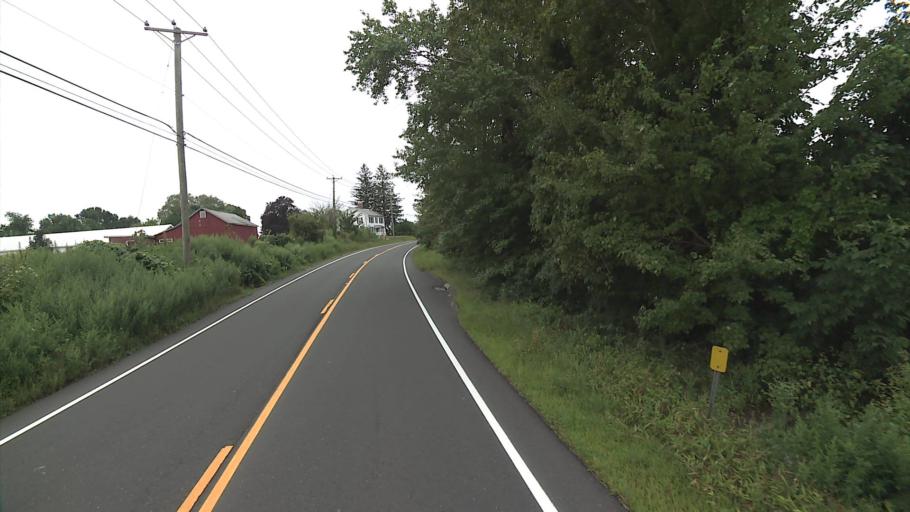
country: US
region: Connecticut
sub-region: New London County
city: Colchester
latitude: 41.5331
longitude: -72.2986
